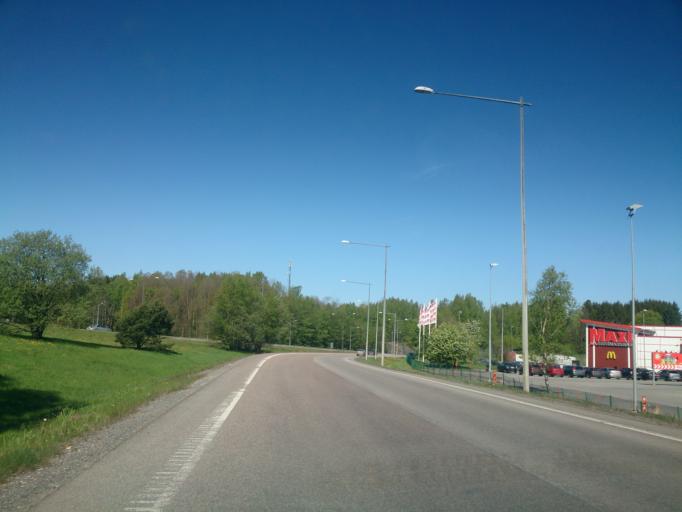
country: SE
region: Stockholm
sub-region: Haninge Kommun
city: Haninge
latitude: 59.1800
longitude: 18.1573
